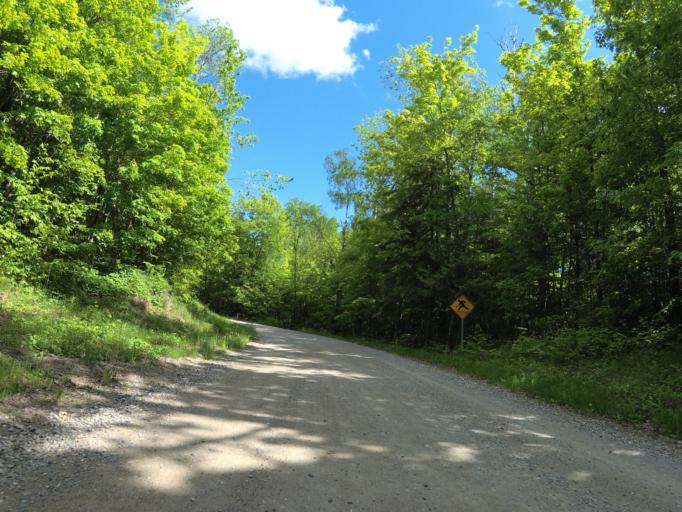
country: CA
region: Ontario
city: Renfrew
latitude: 45.0412
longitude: -76.8194
